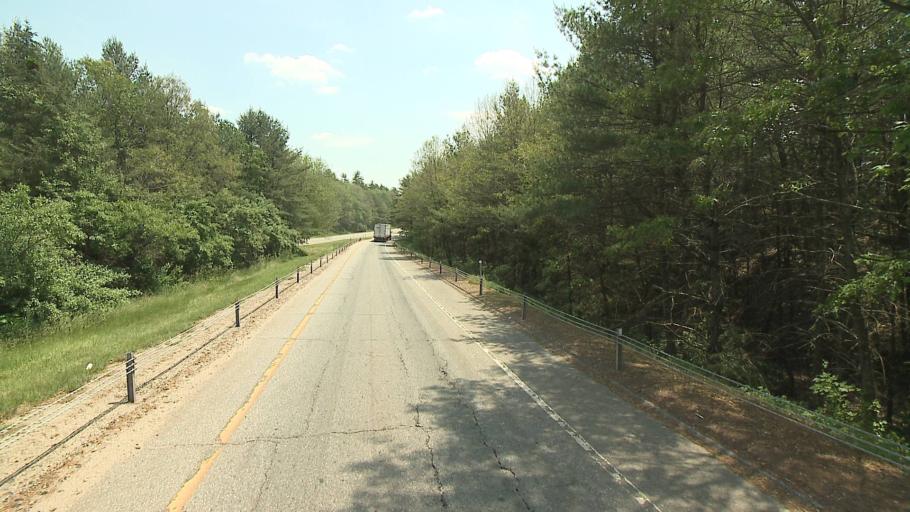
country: US
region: Connecticut
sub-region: Windham County
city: Killingly Center
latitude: 41.8662
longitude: -71.8898
